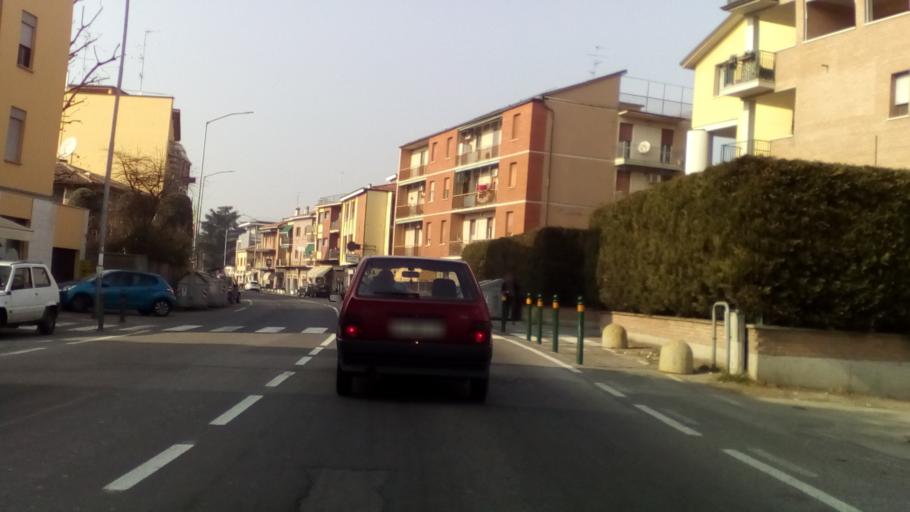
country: IT
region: Emilia-Romagna
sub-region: Provincia di Modena
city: Modena
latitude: 44.6319
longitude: 10.9403
